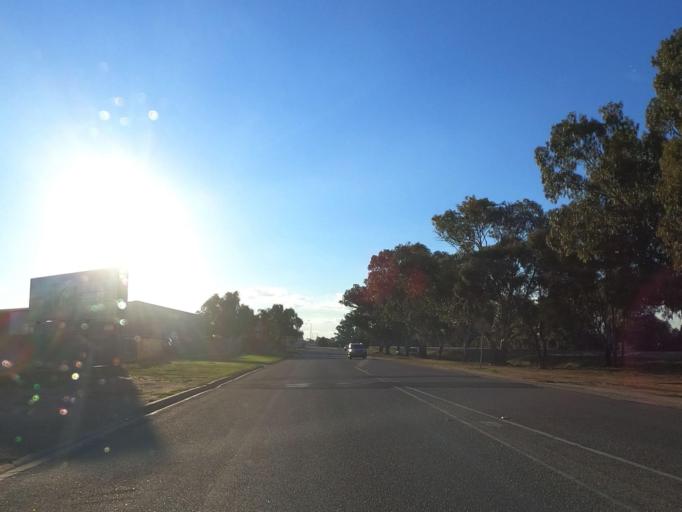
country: AU
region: Victoria
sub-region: Swan Hill
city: Swan Hill
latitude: -35.3295
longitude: 143.5555
